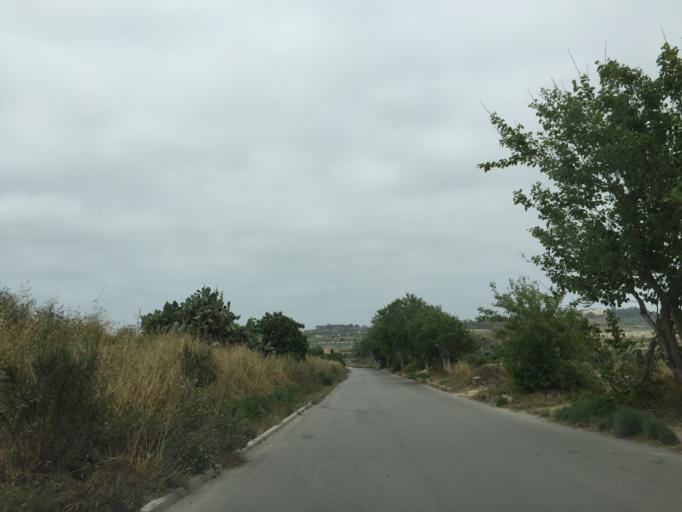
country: MT
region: Ir-Rabat
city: Rabat
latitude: 35.8866
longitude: 14.3821
